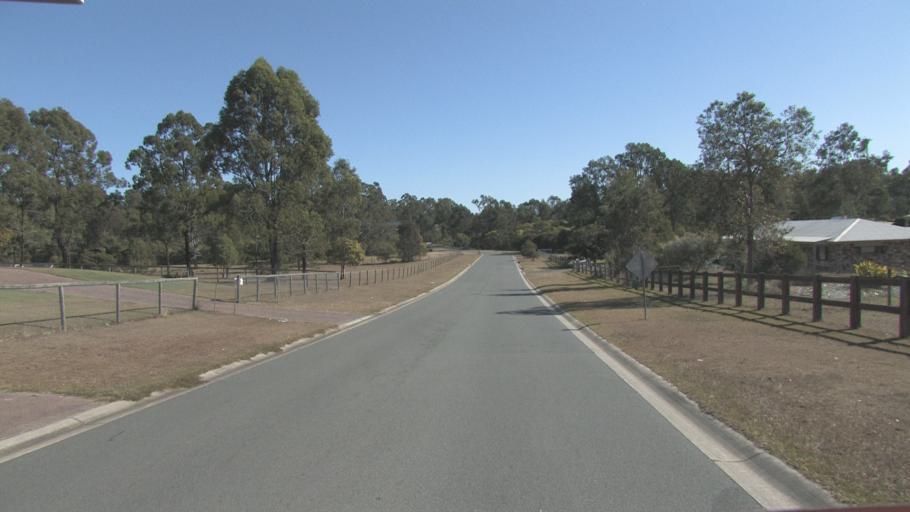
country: AU
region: Queensland
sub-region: Logan
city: Cedar Vale
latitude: -27.8570
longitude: 153.0417
